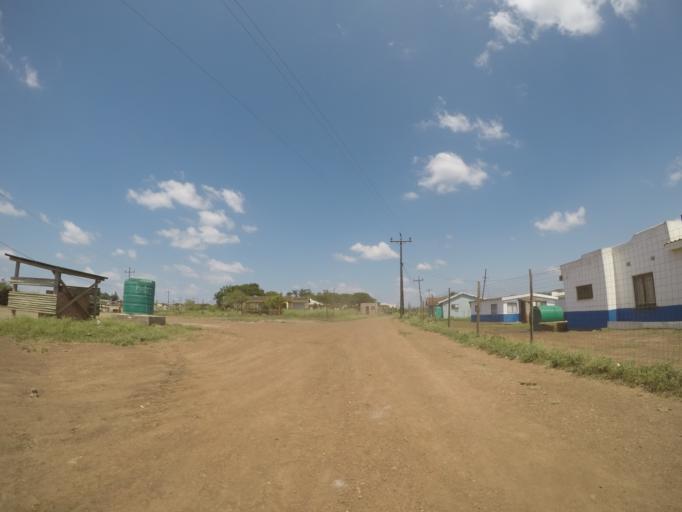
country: ZA
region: KwaZulu-Natal
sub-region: uThungulu District Municipality
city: Empangeni
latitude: -28.6020
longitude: 31.7421
